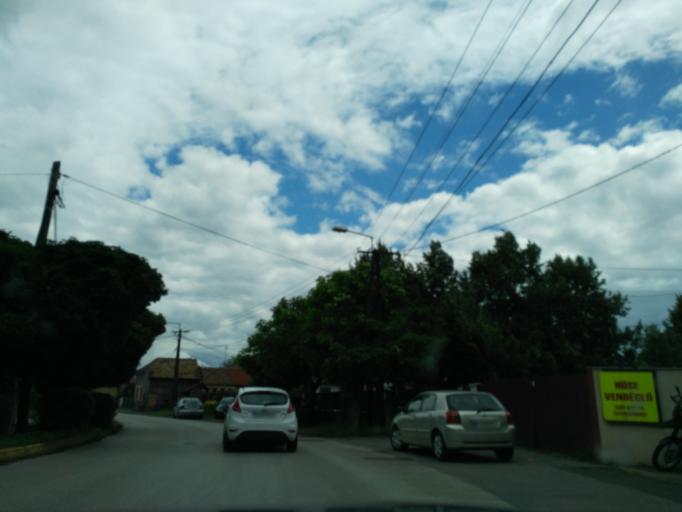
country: HU
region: Hajdu-Bihar
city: Debrecen
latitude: 47.5417
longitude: 21.6436
